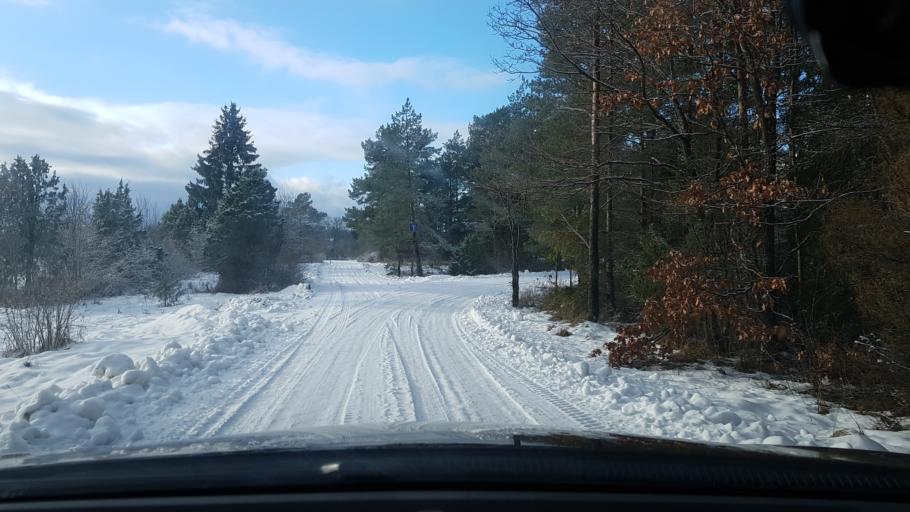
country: EE
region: Harju
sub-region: Keila linn
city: Keila
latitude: 59.2820
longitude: 24.2622
